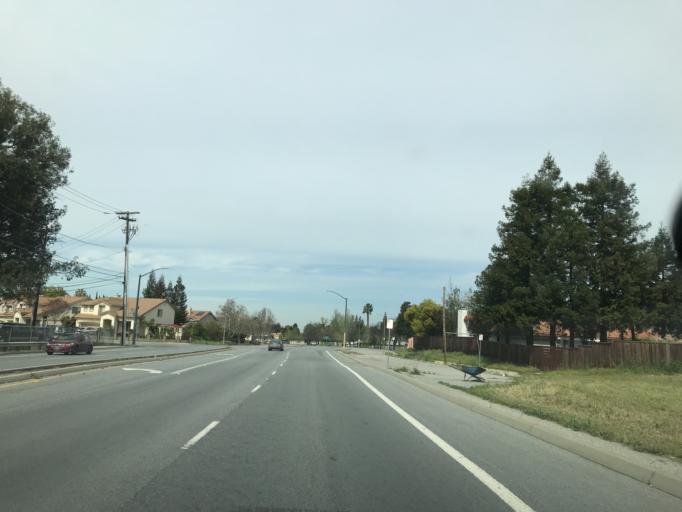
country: US
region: California
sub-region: Santa Clara County
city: Seven Trees
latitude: 37.3113
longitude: -121.7871
